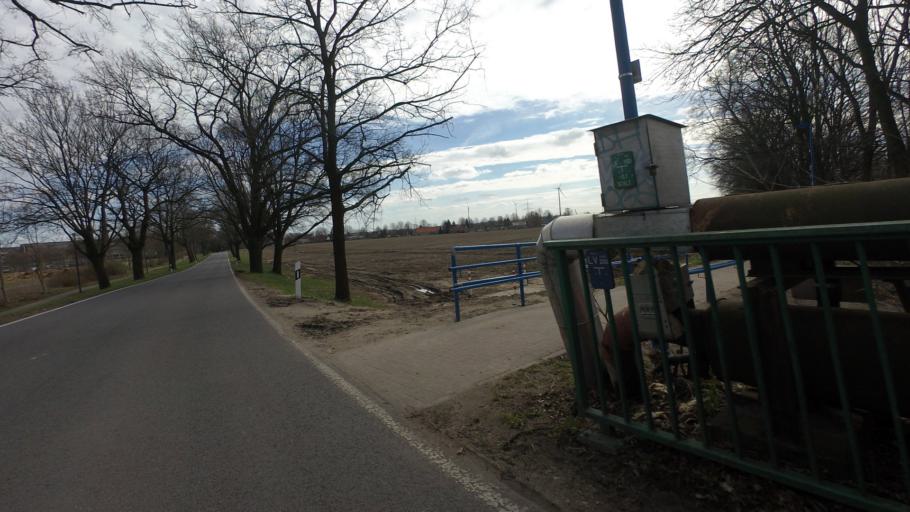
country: DE
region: Berlin
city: Buchholz
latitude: 52.6566
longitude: 13.4295
